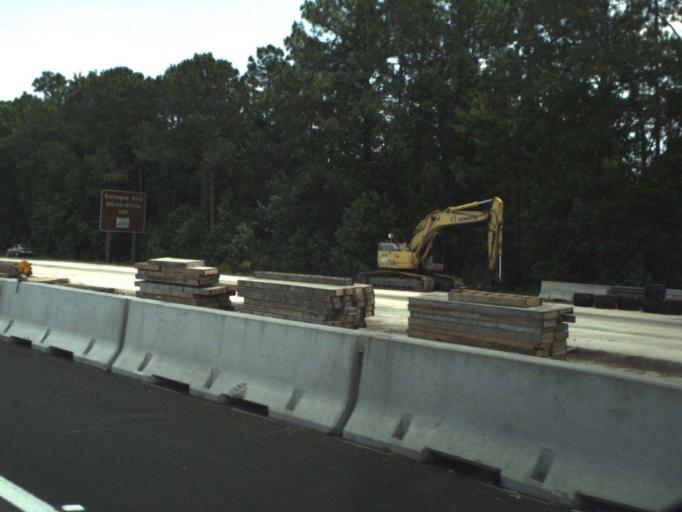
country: US
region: Florida
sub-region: Volusia County
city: South Daytona
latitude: 29.1495
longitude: -81.0897
